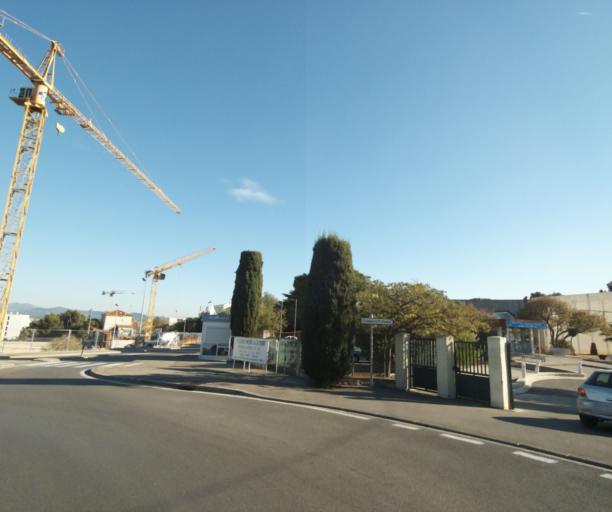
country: FR
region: Provence-Alpes-Cote d'Azur
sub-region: Departement des Bouches-du-Rhone
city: La Ciotat
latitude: 43.1841
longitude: 5.5993
